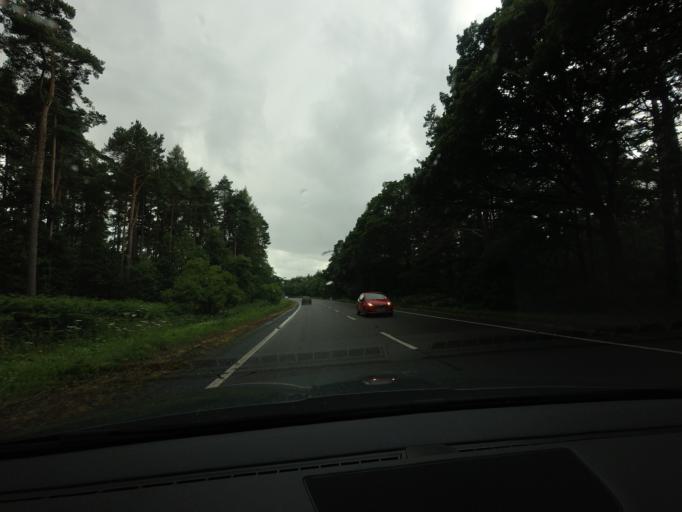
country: GB
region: Scotland
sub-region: Highland
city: Fortrose
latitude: 57.5276
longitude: -4.0561
